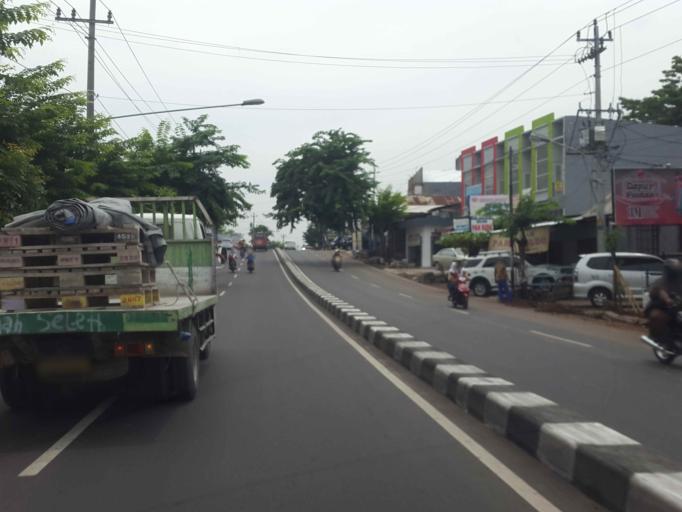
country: ID
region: Central Java
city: Semarang
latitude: -7.0163
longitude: 110.4542
